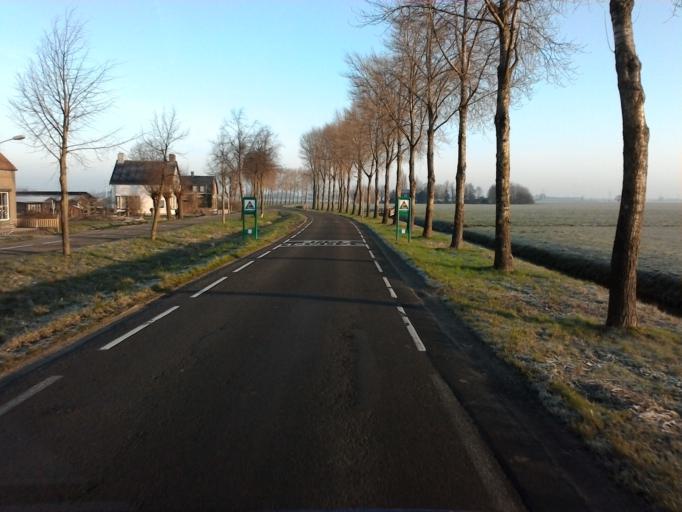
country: NL
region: South Holland
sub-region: Gemeente Gorinchem
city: Gorinchem
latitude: 51.8500
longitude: 4.9576
